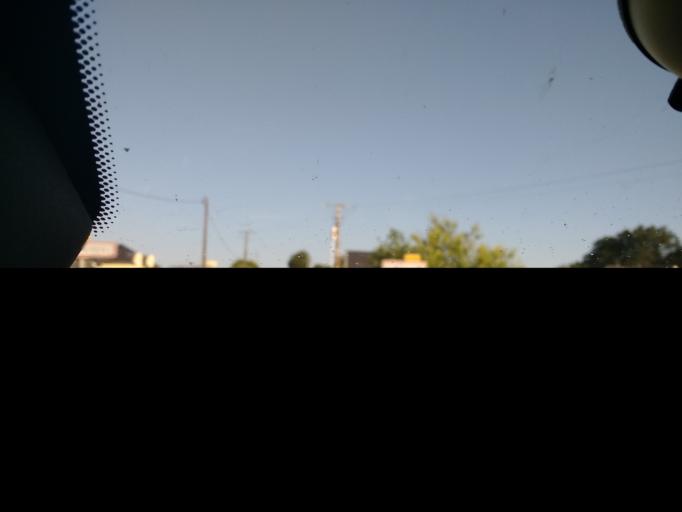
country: FR
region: Brittany
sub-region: Departement du Morbihan
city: Limerzel
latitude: 47.6400
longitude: -2.3594
